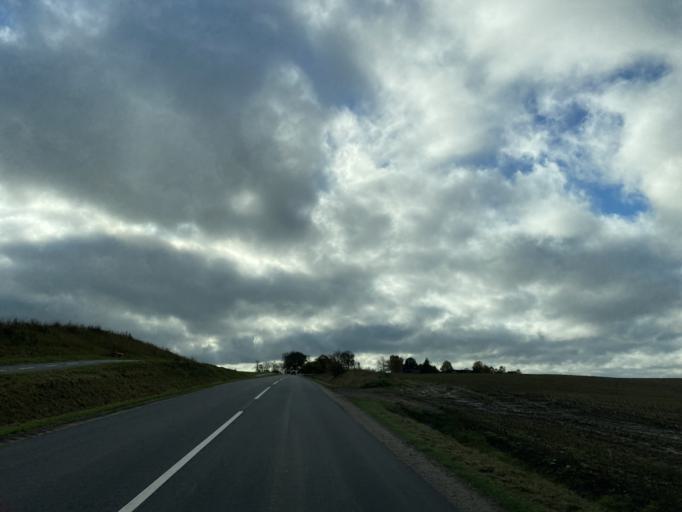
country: DK
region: Central Jutland
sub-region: Favrskov Kommune
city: Hammel
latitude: 56.2495
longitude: 9.8267
